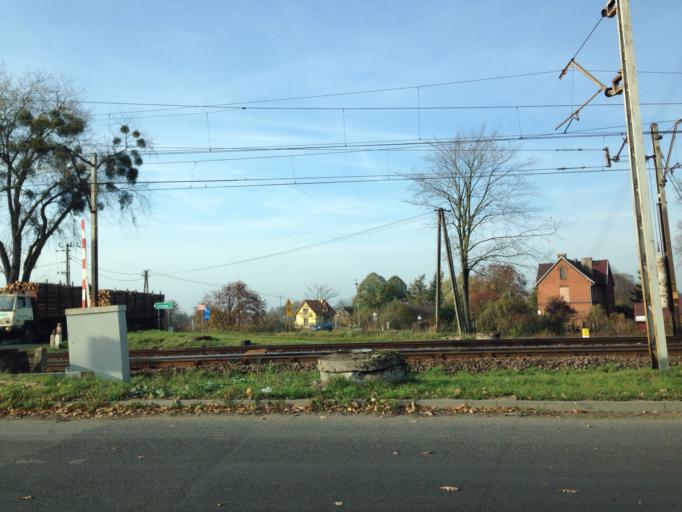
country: PL
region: Kujawsko-Pomorskie
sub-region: Powiat swiecki
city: Pruszcz
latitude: 53.2866
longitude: 18.1245
